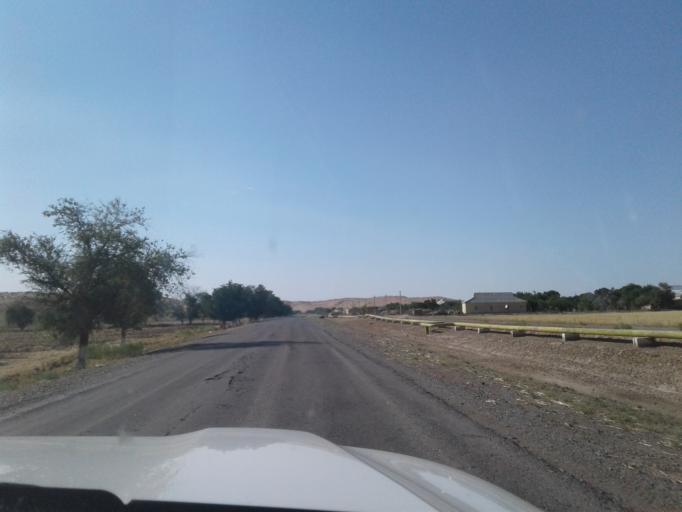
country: TM
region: Mary
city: Yoloeten
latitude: 36.7005
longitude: 62.4579
